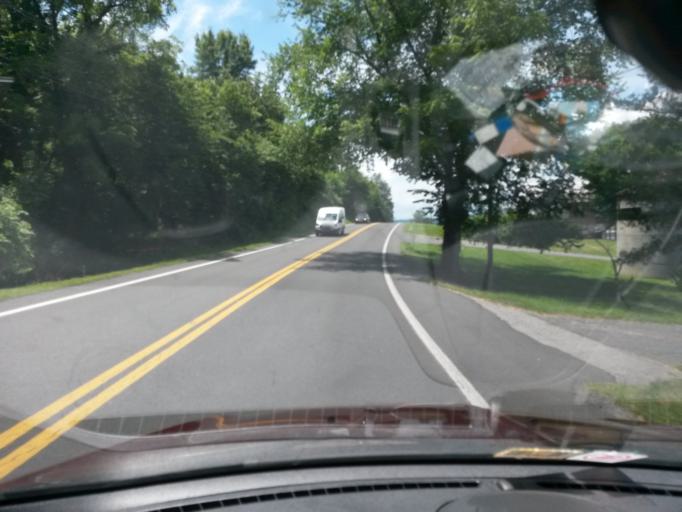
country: US
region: West Virginia
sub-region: Hardy County
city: Moorefield
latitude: 39.0390
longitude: -78.9859
